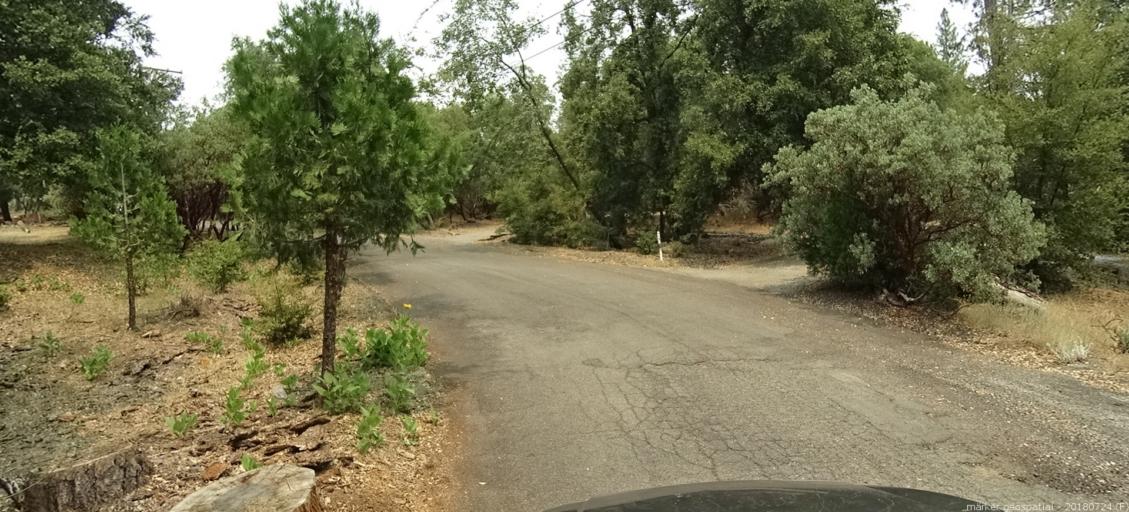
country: US
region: California
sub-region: Madera County
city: Oakhurst
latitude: 37.3204
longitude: -119.5866
